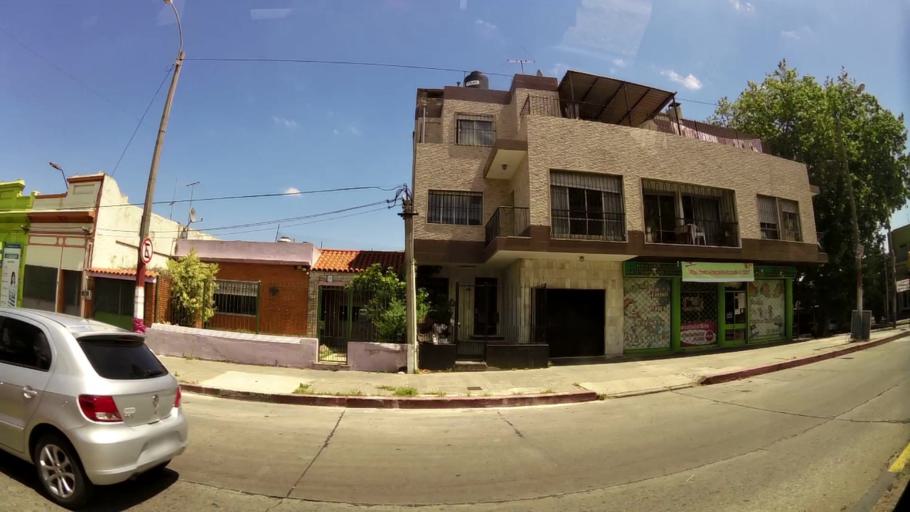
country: UY
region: Montevideo
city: Montevideo
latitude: -34.8581
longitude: -56.2258
